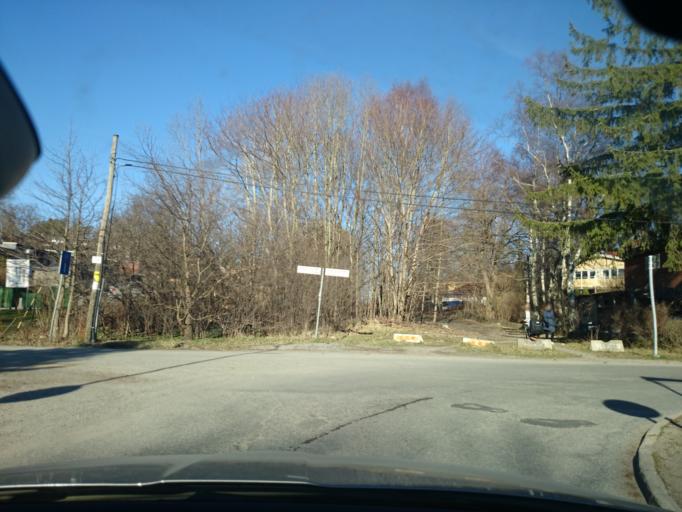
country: SE
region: Stockholm
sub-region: Huddinge Kommun
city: Segeltorp
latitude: 59.2773
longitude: 17.9549
